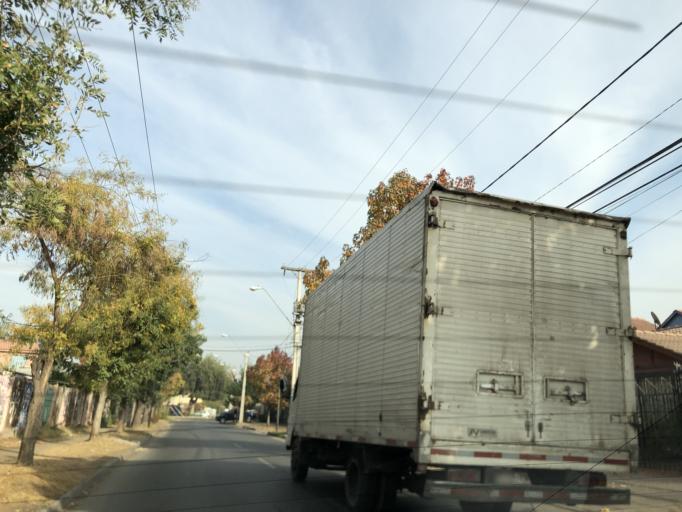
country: CL
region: Santiago Metropolitan
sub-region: Provincia de Cordillera
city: Puente Alto
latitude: -33.5882
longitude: -70.5617
